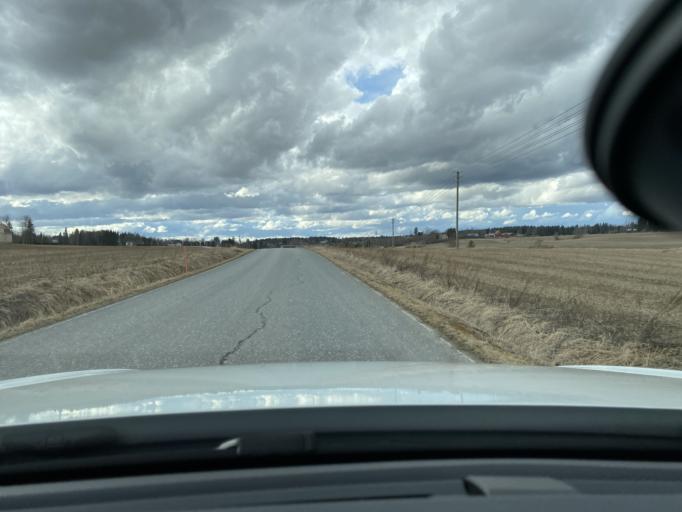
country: FI
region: Pirkanmaa
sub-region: Lounais-Pirkanmaa
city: Punkalaidun
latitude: 61.1166
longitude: 23.0711
